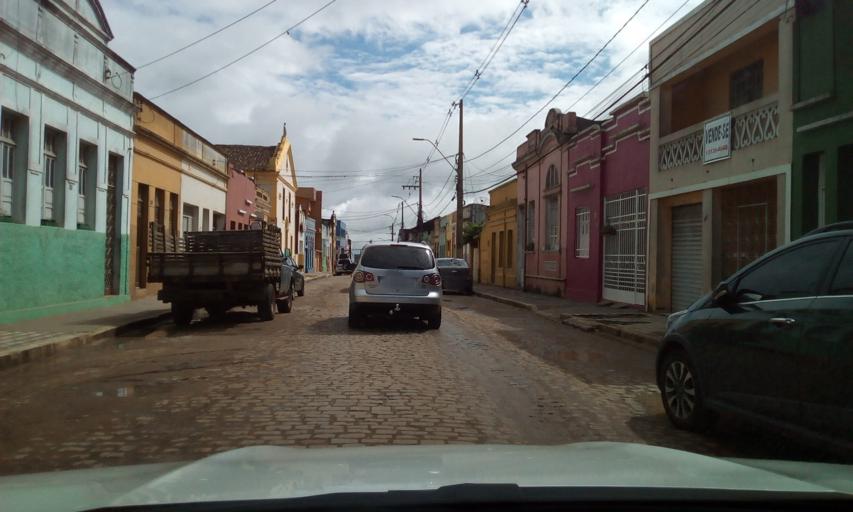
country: BR
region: Paraiba
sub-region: Areia
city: Areia
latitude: -6.9677
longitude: -35.7012
